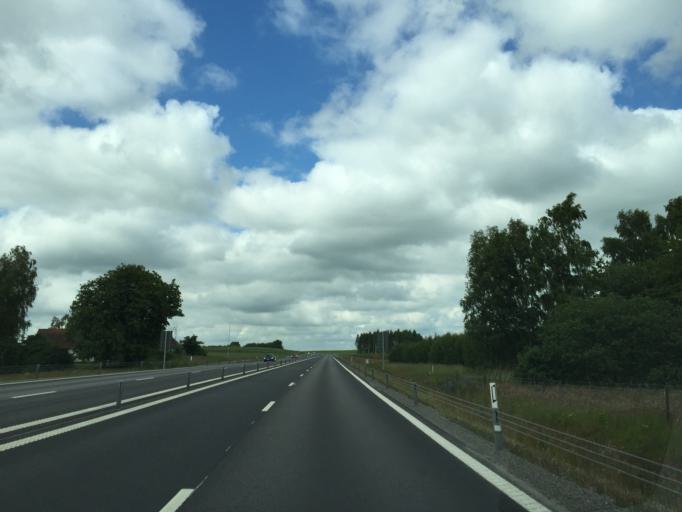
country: SE
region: Skane
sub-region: Svedala Kommun
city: Klagerup
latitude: 55.5639
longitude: 13.2554
